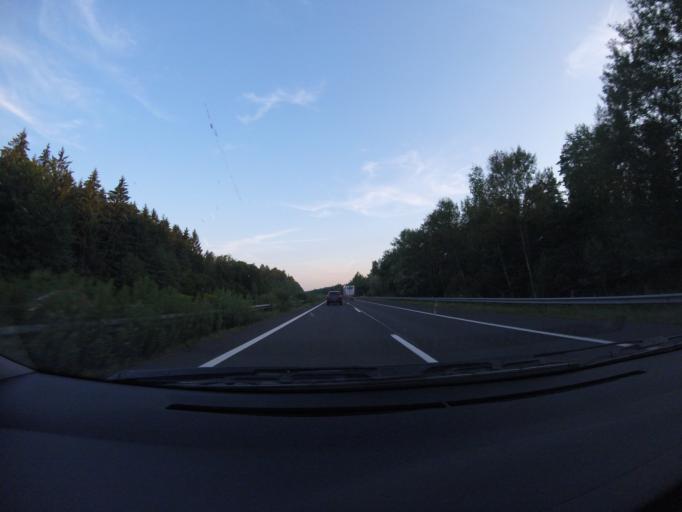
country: AT
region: Styria
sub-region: Politischer Bezirk Hartberg-Fuerstenfeld
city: Bad Waltersdorf
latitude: 47.1348
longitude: 15.9867
